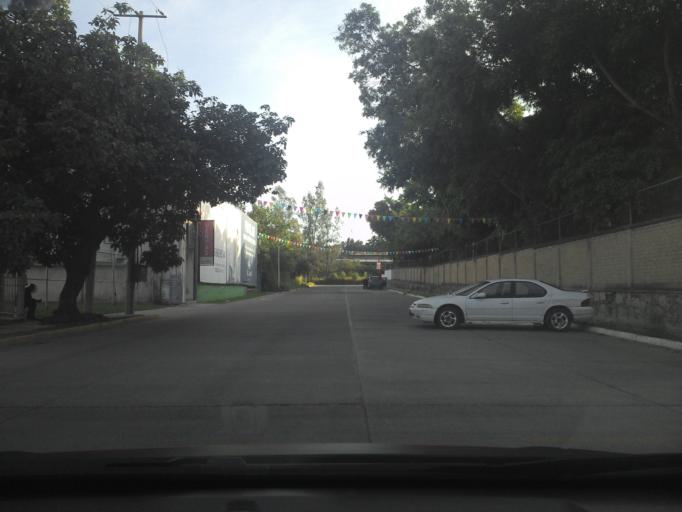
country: MX
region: Jalisco
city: Tlaquepaque
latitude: 20.6175
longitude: -103.3260
